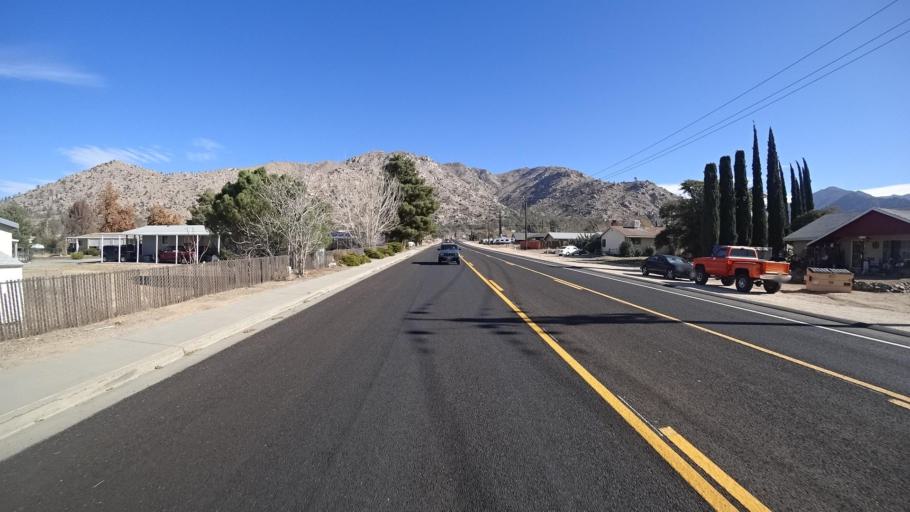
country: US
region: California
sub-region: Kern County
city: Lake Isabella
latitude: 35.6167
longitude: -118.4705
